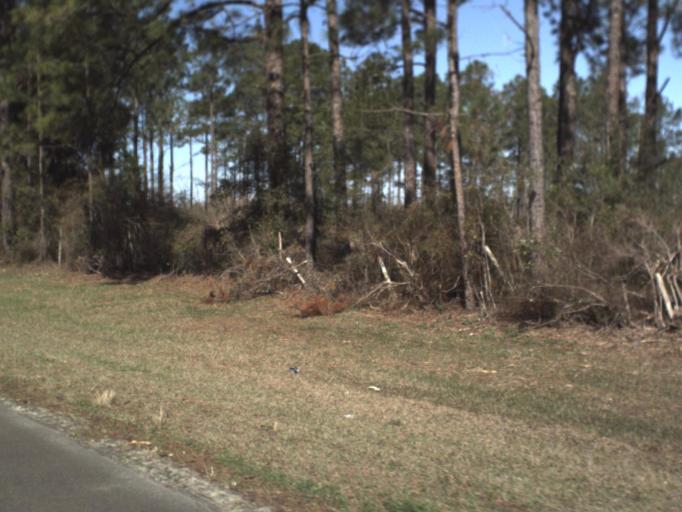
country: US
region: Florida
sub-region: Gulf County
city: Wewahitchka
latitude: 30.1331
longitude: -85.3511
